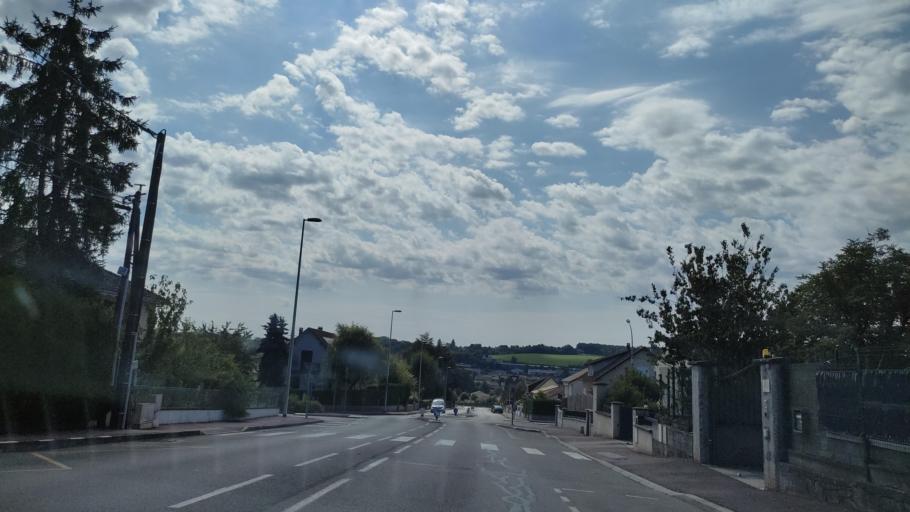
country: FR
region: Limousin
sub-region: Departement de la Haute-Vienne
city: Isle
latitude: 45.8263
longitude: 1.2031
